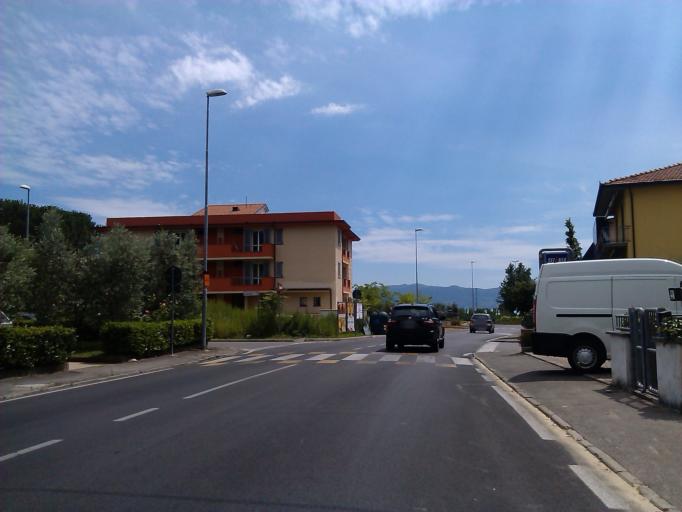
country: IT
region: Tuscany
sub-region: Provincia di Pistoia
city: Montale
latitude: 43.9326
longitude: 11.0246
